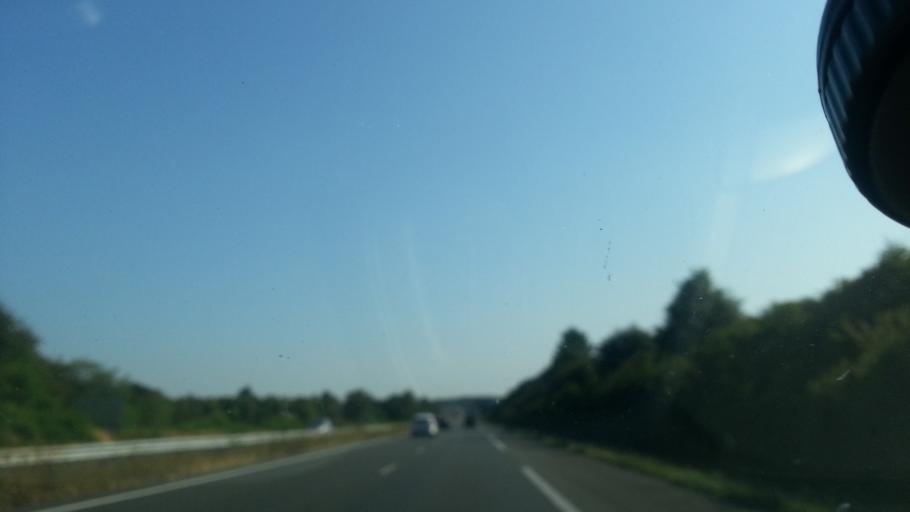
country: FR
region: Poitou-Charentes
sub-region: Departement de la Vienne
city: Dange-Saint-Romain
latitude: 46.9209
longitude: 0.5340
